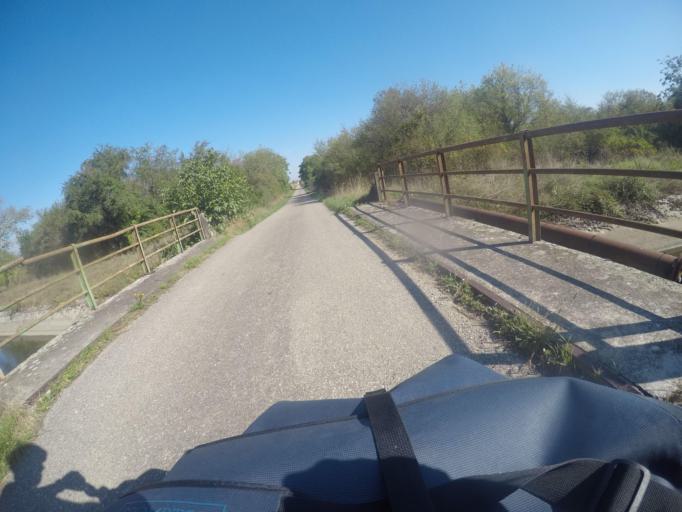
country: FR
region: Alsace
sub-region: Departement du Haut-Rhin
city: Ottmarsheim
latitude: 47.7800
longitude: 7.5056
